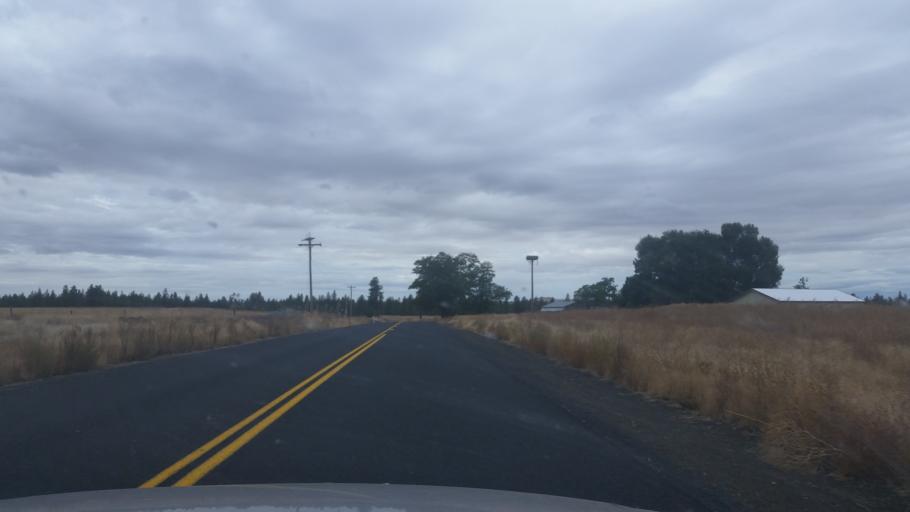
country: US
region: Washington
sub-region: Spokane County
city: Medical Lake
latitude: 47.5153
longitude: -117.7406
